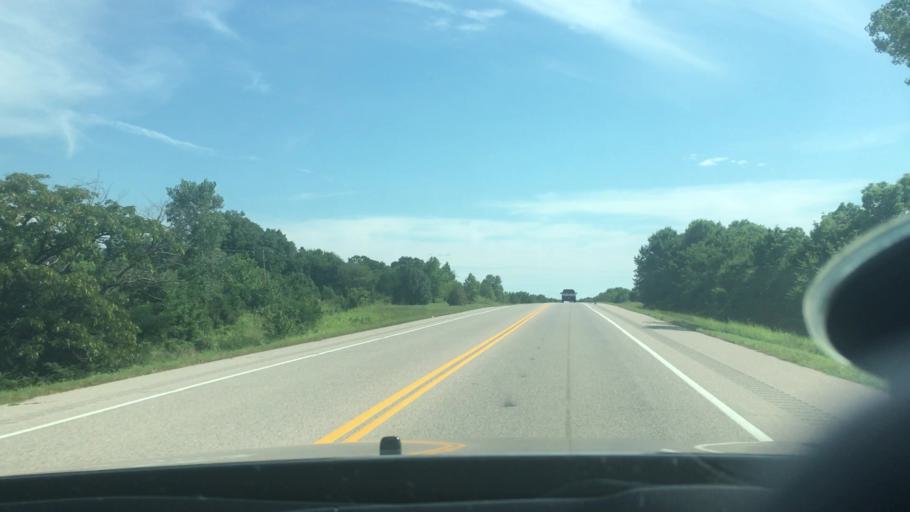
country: US
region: Oklahoma
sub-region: Seminole County
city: Konawa
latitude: 35.0166
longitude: -96.6785
